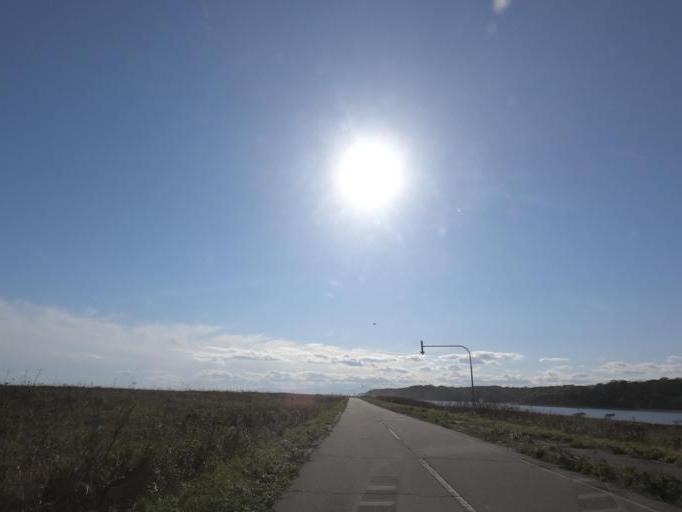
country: JP
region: Hokkaido
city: Obihiro
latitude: 42.5832
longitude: 143.5324
